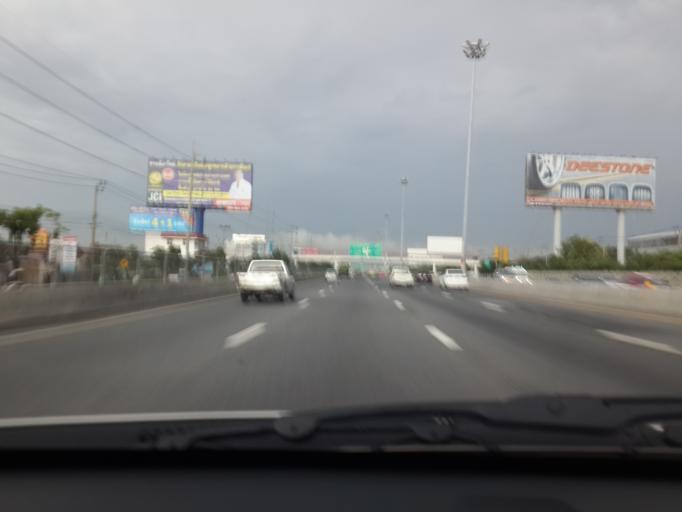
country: TH
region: Bangkok
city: Saphan Sung
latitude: 13.7342
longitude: 100.6893
